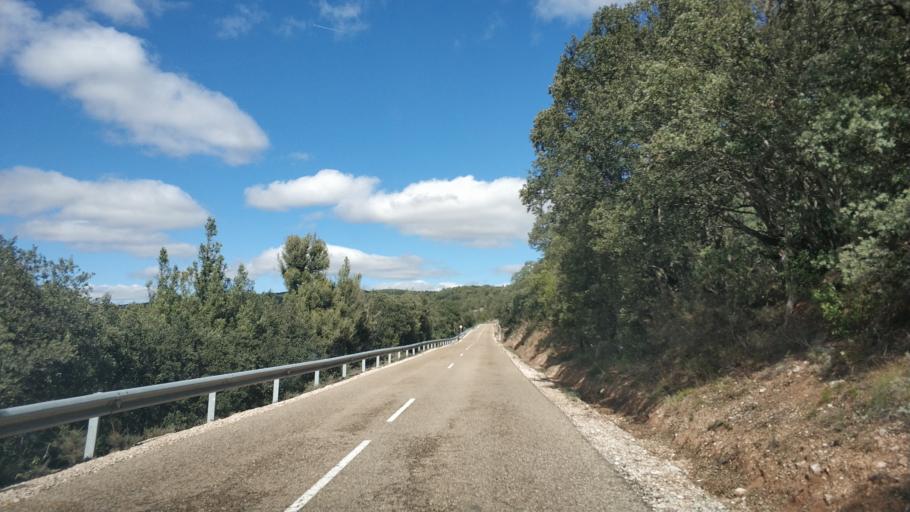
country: ES
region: Castille and Leon
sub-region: Provincia de Burgos
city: Retuerta
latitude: 42.0403
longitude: -3.4774
